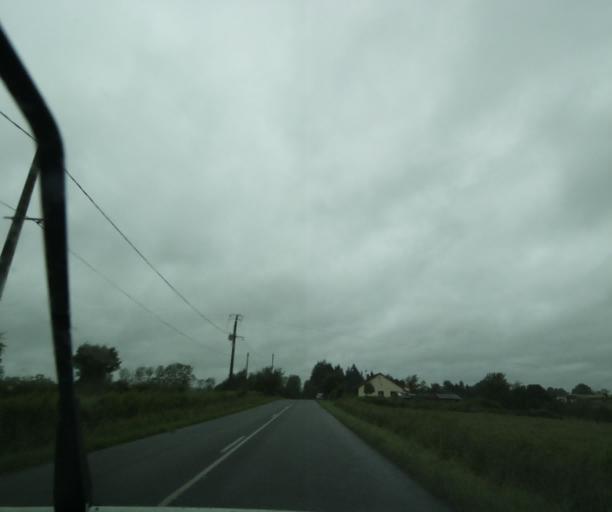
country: FR
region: Bourgogne
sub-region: Departement de Saone-et-Loire
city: Palinges
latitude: 46.5561
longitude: 4.2377
